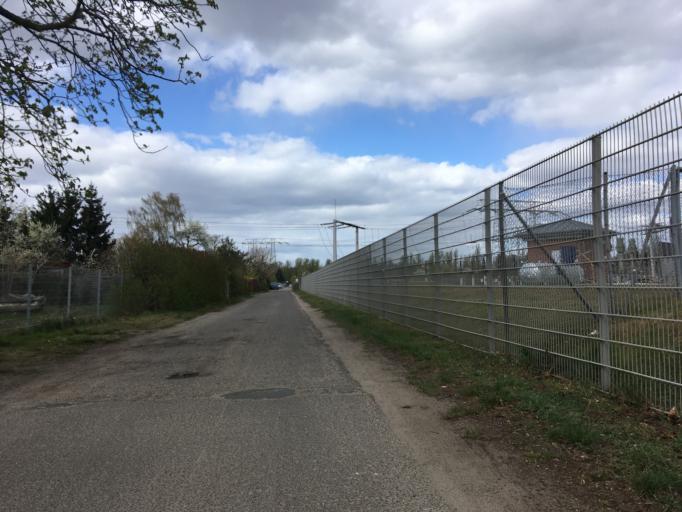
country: DE
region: Berlin
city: Baumschulenweg
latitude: 52.4733
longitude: 13.5043
